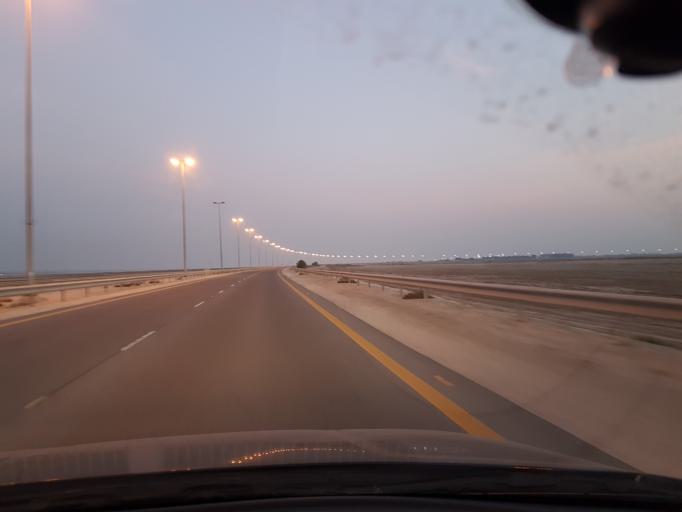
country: BH
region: Central Governorate
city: Dar Kulayb
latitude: 26.0086
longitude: 50.4842
